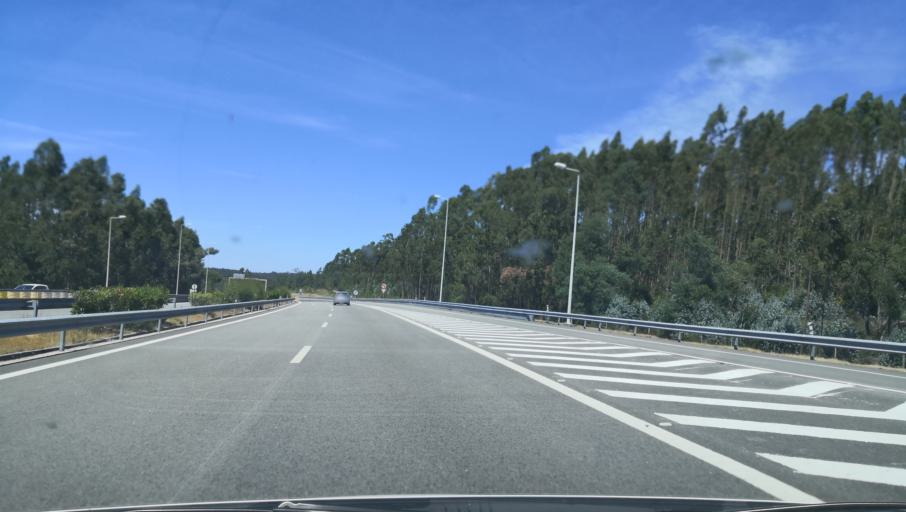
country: PT
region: Coimbra
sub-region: Montemor-O-Velho
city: Montemor-o-Velho
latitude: 40.2049
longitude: -8.6747
